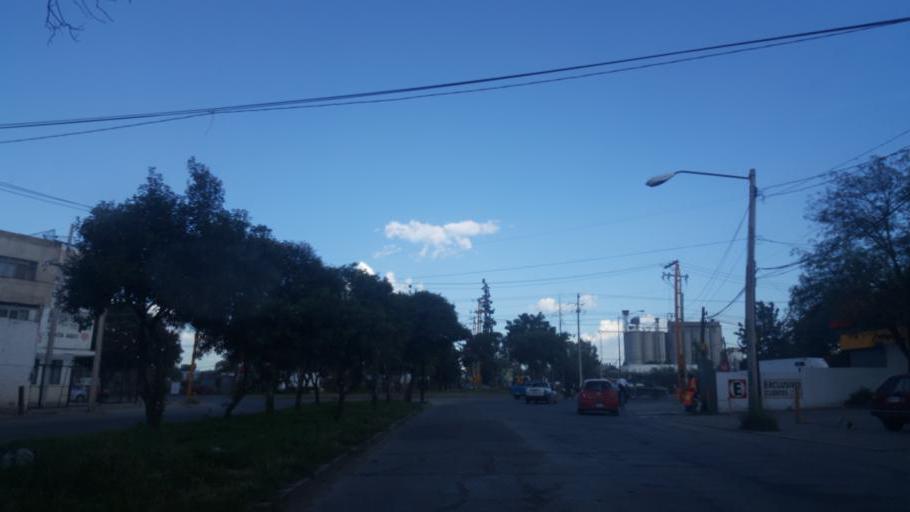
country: MX
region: Guanajuato
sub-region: Leon
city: San Jose de Duran (Los Troncoso)
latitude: 21.0952
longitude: -101.6960
